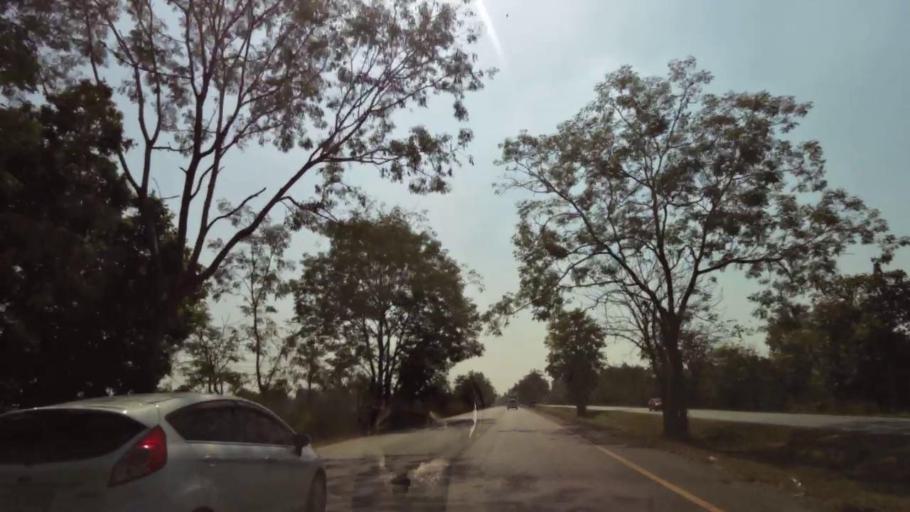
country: TH
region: Phichit
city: Wachira Barami
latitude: 16.3658
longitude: 100.1313
